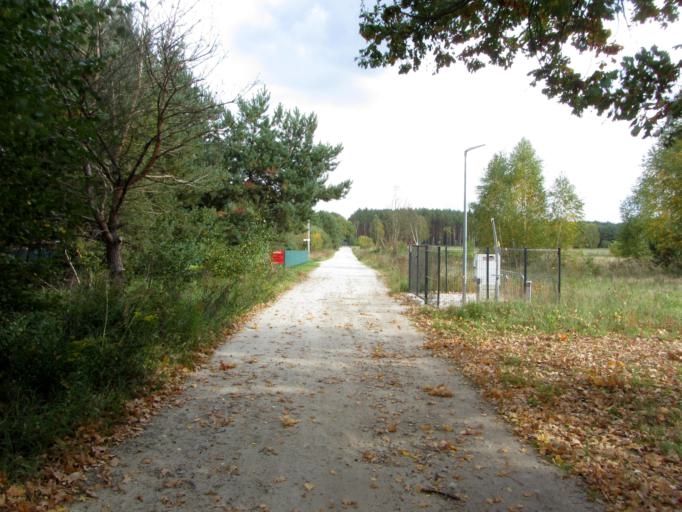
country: PL
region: Lubusz
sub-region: Powiat wschowski
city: Slawa
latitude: 51.8724
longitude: 15.9992
